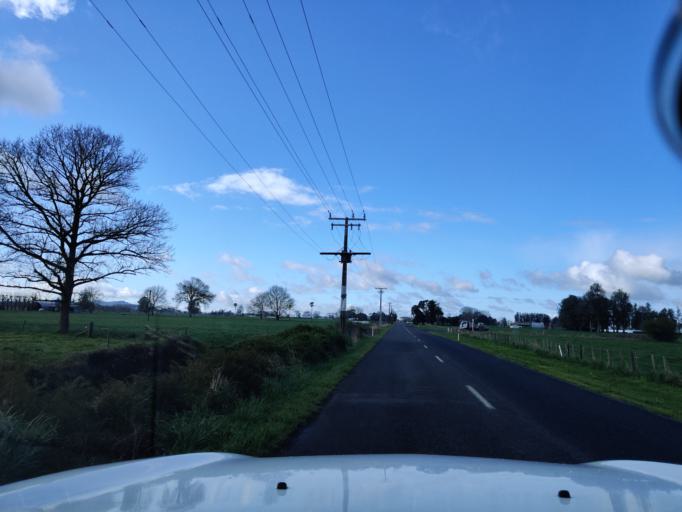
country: NZ
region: Waikato
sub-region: Waikato District
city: Ngaruawahia
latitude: -37.5783
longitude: 175.2722
